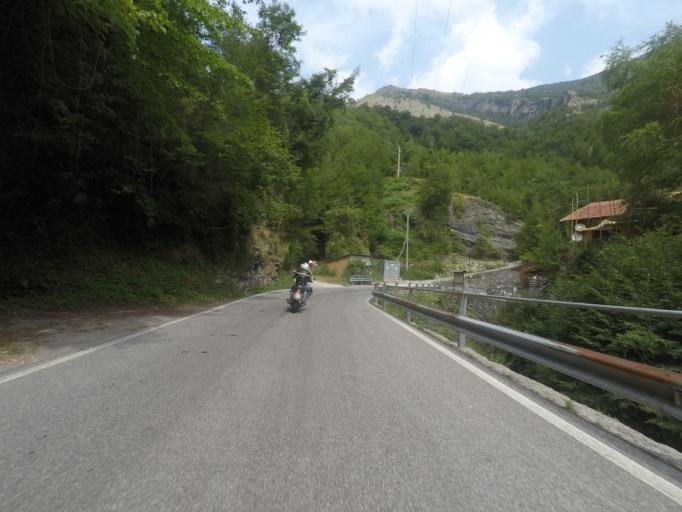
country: IT
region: Tuscany
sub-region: Provincia di Lucca
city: Careggine
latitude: 44.0659
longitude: 10.3114
